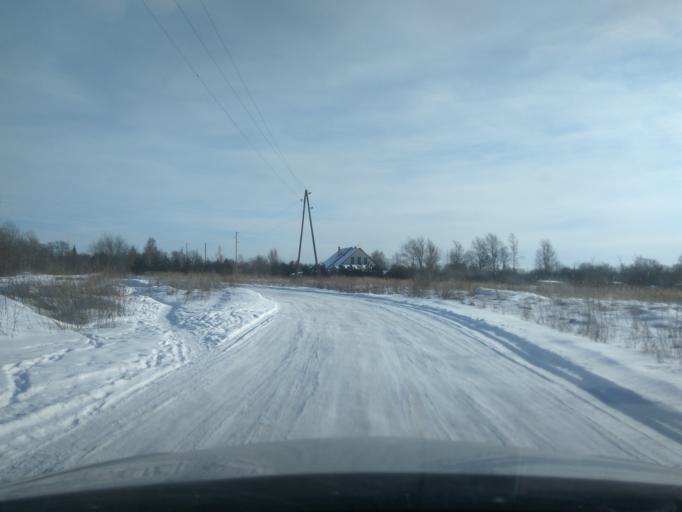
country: LV
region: Kuldigas Rajons
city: Kuldiga
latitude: 56.9825
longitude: 21.9554
